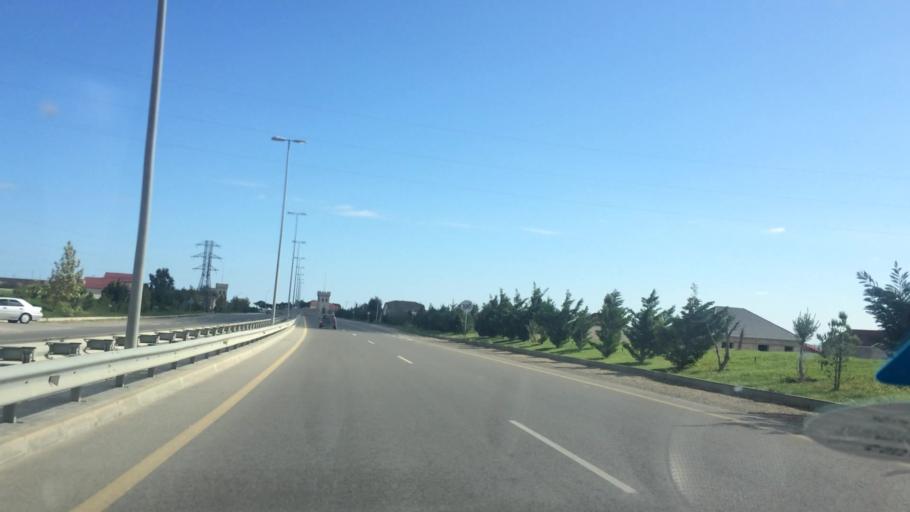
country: AZ
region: Baki
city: Zyrya
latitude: 40.3981
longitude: 50.3292
